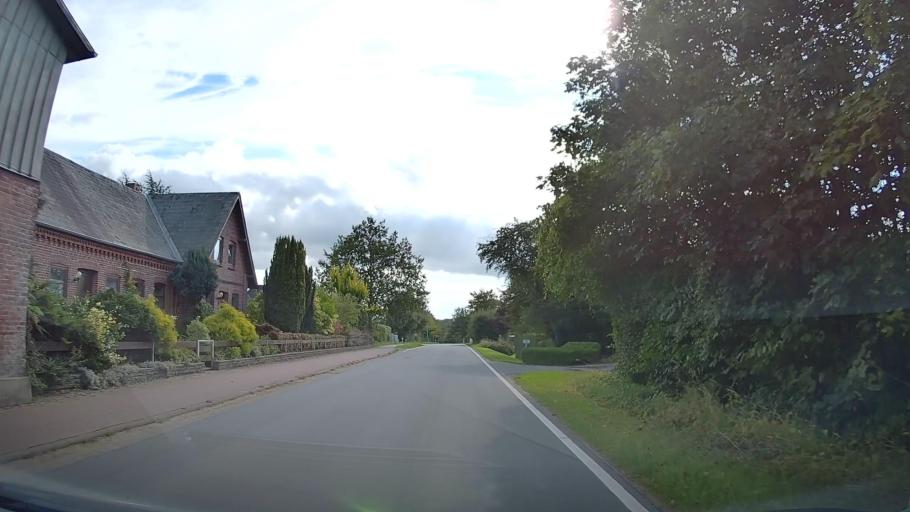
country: DE
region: Schleswig-Holstein
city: Westerholz
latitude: 54.8142
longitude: 9.6710
